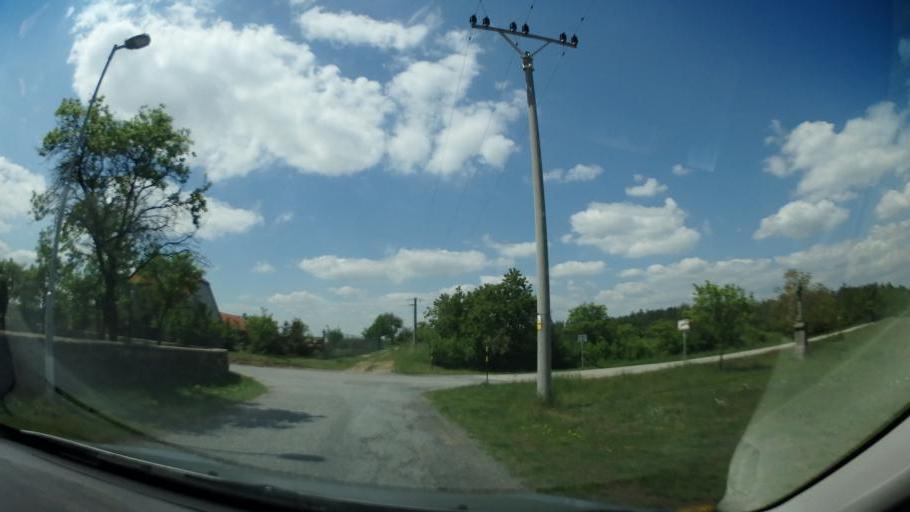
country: CZ
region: Vysocina
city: Hrotovice
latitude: 49.1555
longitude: 16.0773
